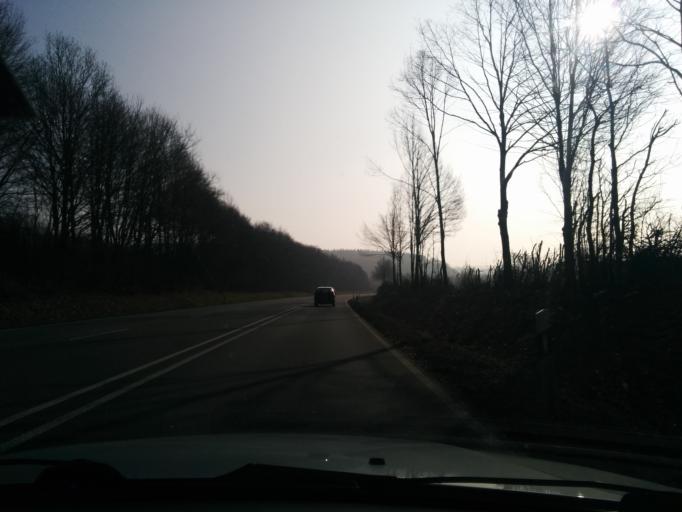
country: DE
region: North Rhine-Westphalia
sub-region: Regierungsbezirk Detmold
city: Nieheim
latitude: 51.7835
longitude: 9.1455
